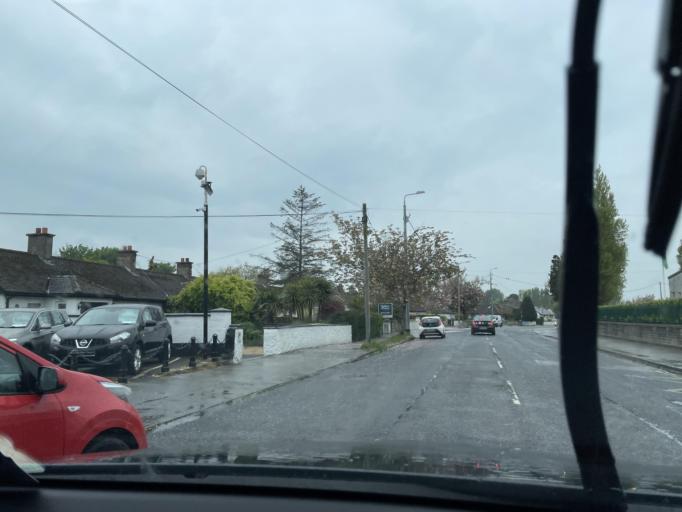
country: IE
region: Leinster
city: Dundrum
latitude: 53.2964
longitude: -6.2639
